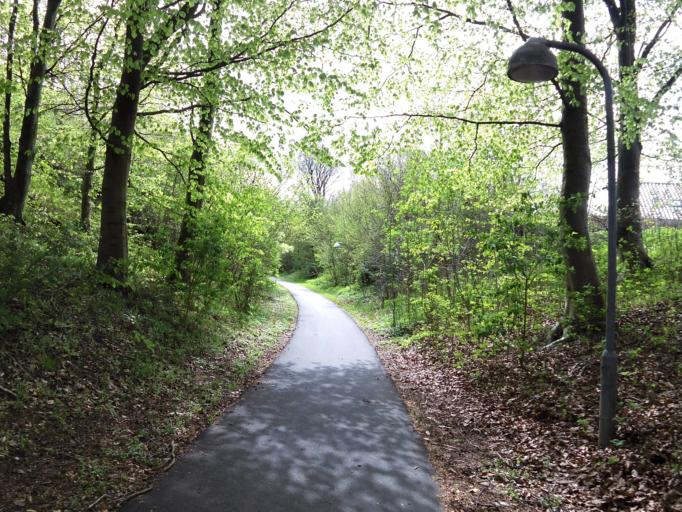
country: DK
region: South Denmark
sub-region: Haderslev Kommune
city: Gram
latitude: 55.2945
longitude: 9.0450
